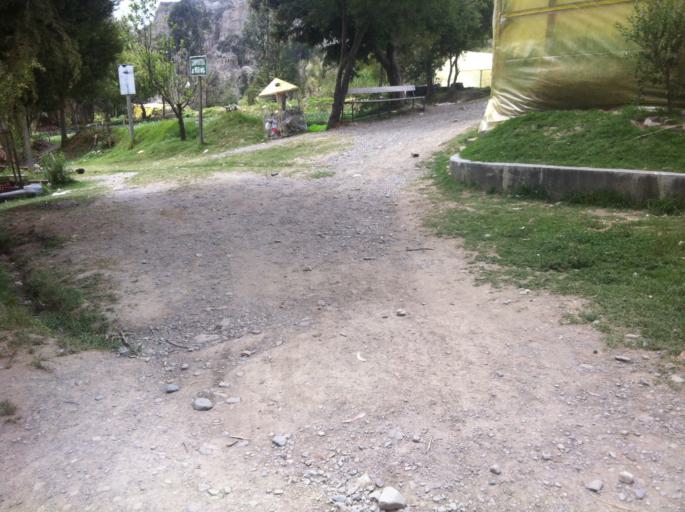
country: BO
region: La Paz
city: La Paz
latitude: -16.5366
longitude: -68.0639
